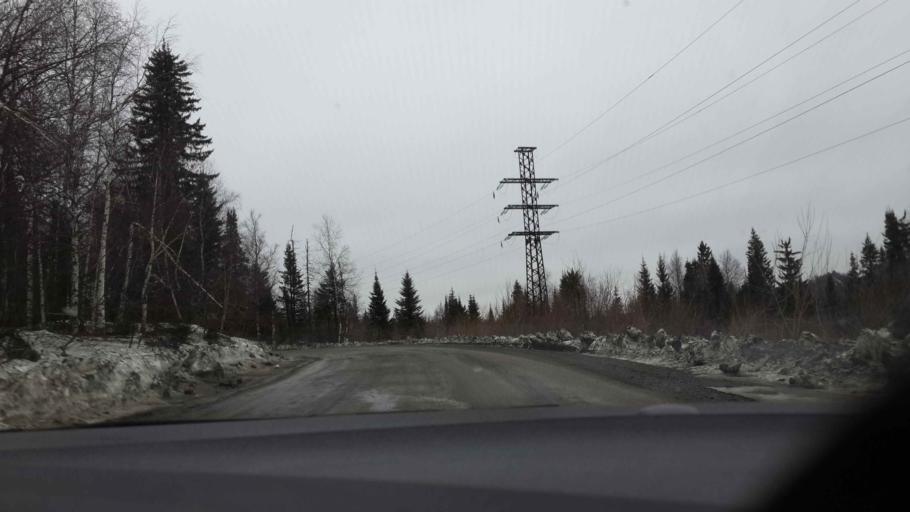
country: RU
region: Chelyabinsk
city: Magnitka
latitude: 55.2678
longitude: 59.6995
